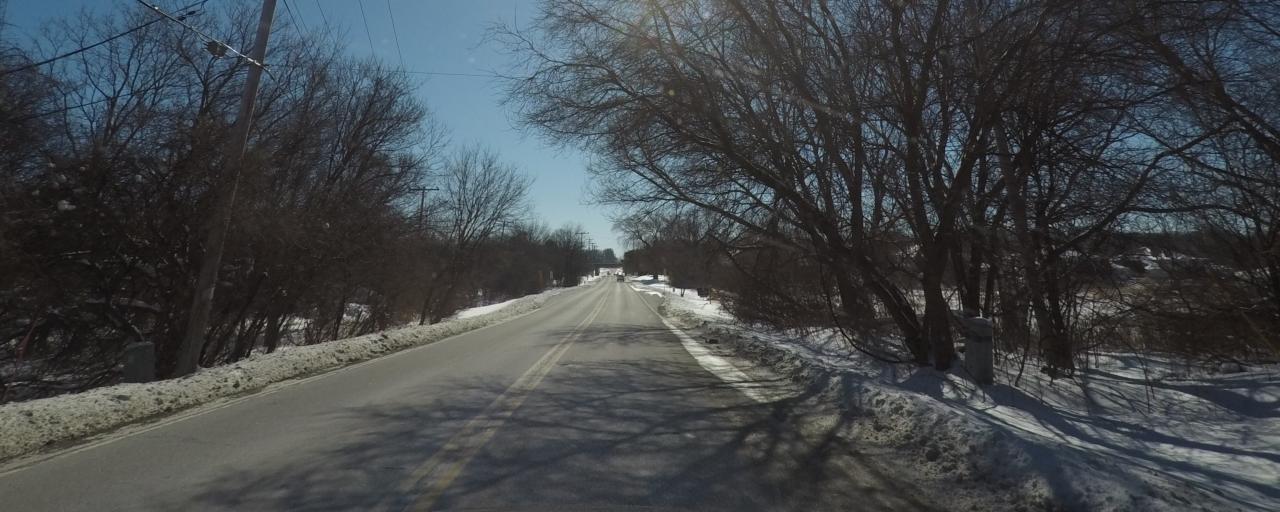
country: US
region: Wisconsin
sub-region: Waukesha County
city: Brookfield
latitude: 43.0322
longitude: -88.1468
